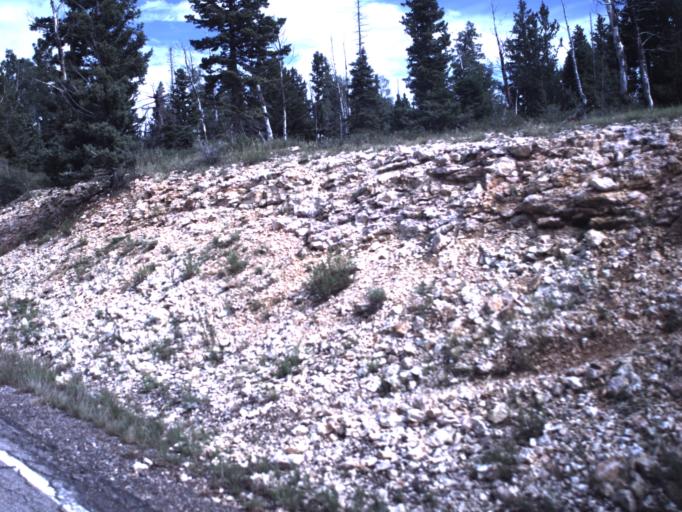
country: US
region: Utah
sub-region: Iron County
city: Parowan
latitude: 37.5277
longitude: -112.7628
